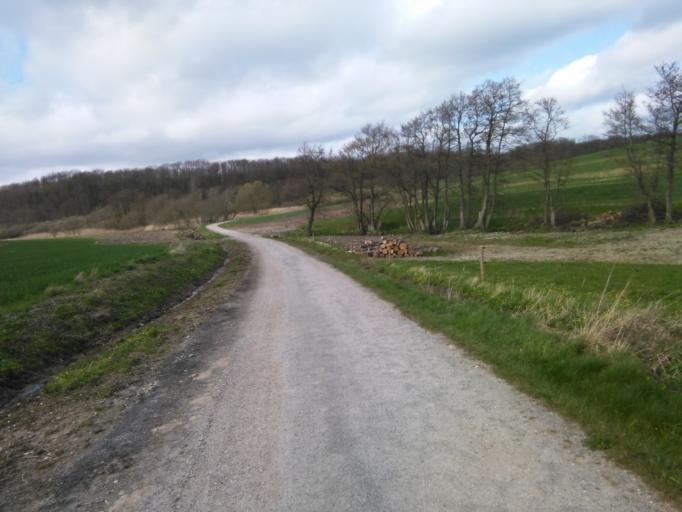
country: DK
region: Central Jutland
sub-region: Arhus Kommune
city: Beder
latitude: 56.0769
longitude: 10.2021
